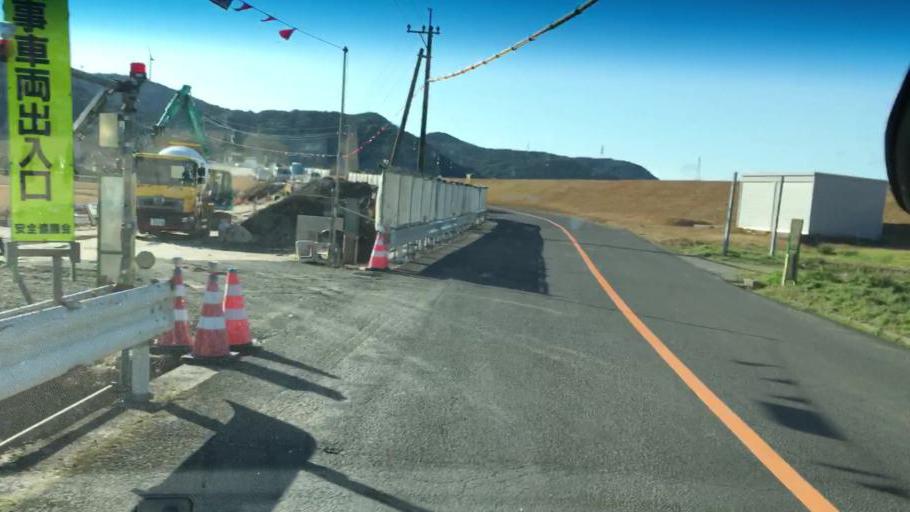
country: JP
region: Kagoshima
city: Satsumasendai
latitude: 31.8294
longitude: 130.2395
